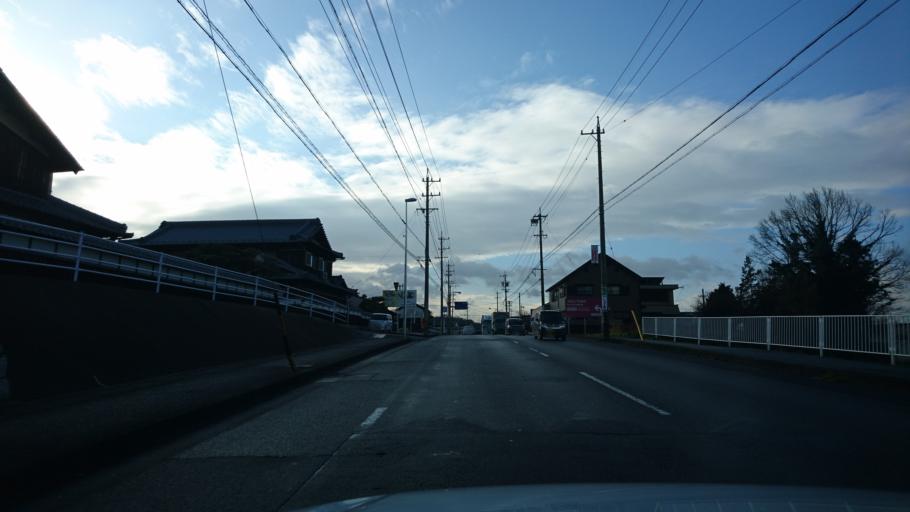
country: JP
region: Mie
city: Ueno-ebisumachi
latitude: 34.7585
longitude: 136.1238
